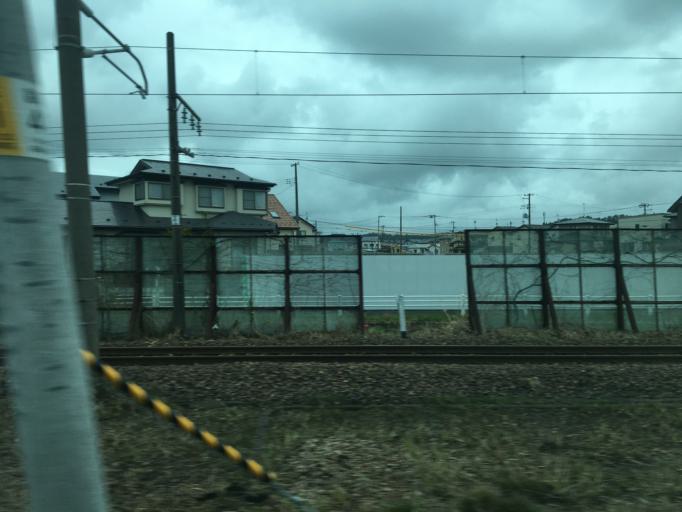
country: JP
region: Akita
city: Akita Shi
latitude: 39.7397
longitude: 140.1094
